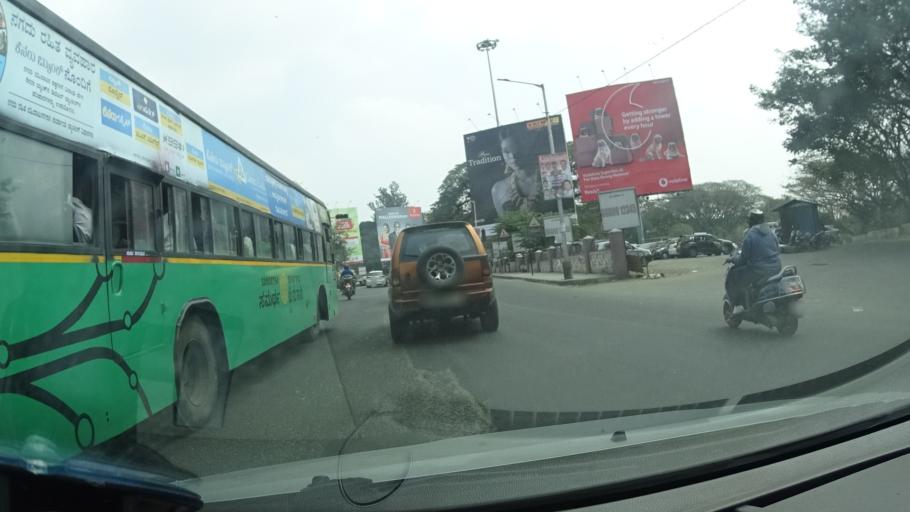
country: IN
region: Karnataka
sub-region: Bangalore Urban
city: Bangalore
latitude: 12.9937
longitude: 77.5973
